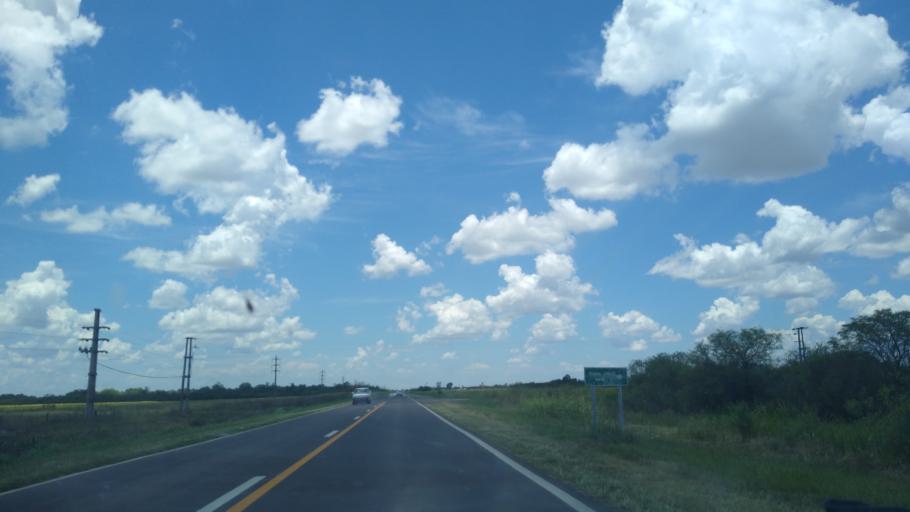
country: AR
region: Chaco
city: Presidencia Roque Saenz Pena
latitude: -26.7437
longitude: -60.3882
